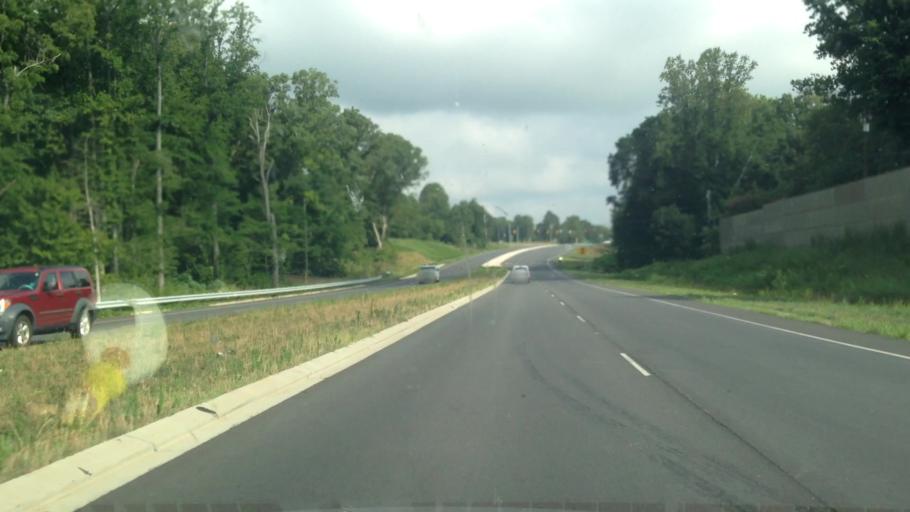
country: US
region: North Carolina
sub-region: Guilford County
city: Summerfield
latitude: 36.2052
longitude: -79.9017
